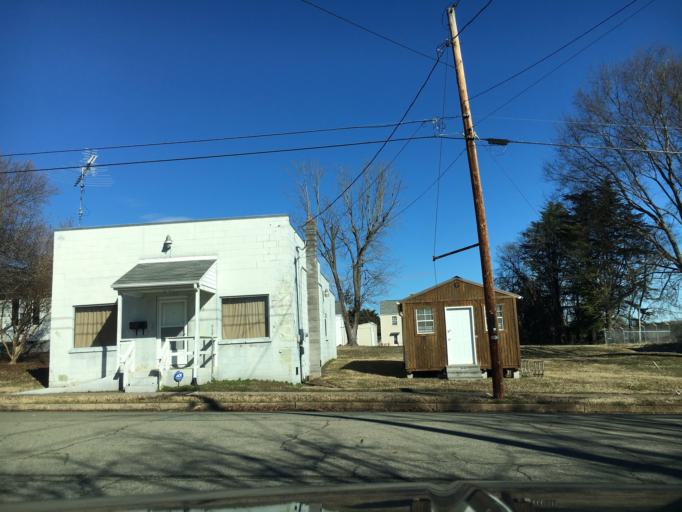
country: US
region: Virginia
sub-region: Halifax County
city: South Boston
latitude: 36.6983
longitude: -78.8833
